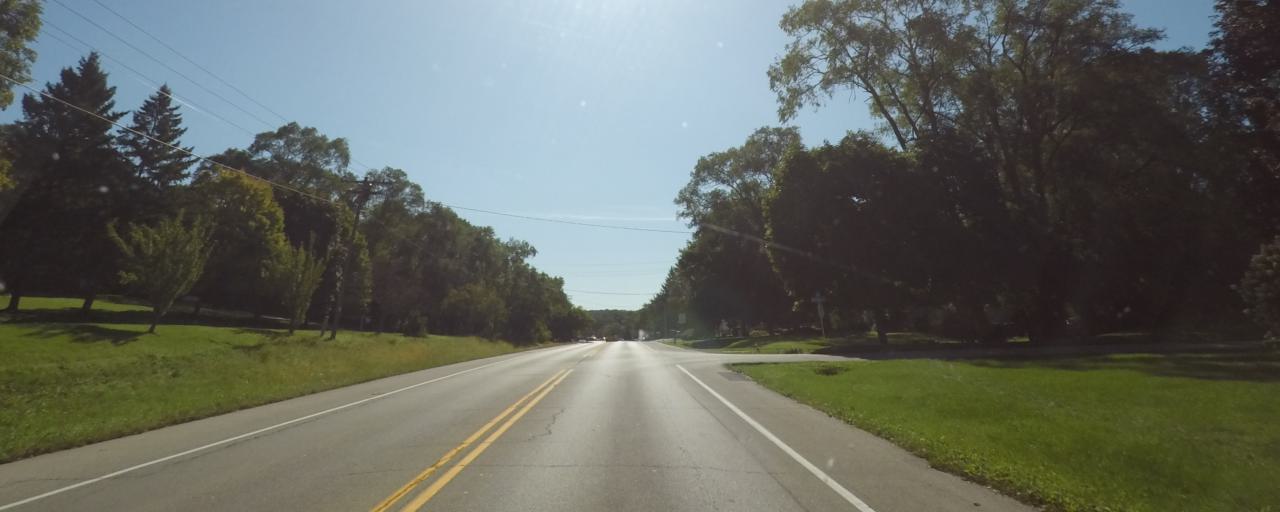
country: US
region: Wisconsin
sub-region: Waukesha County
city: Waukesha
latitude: 42.9995
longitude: -88.2118
